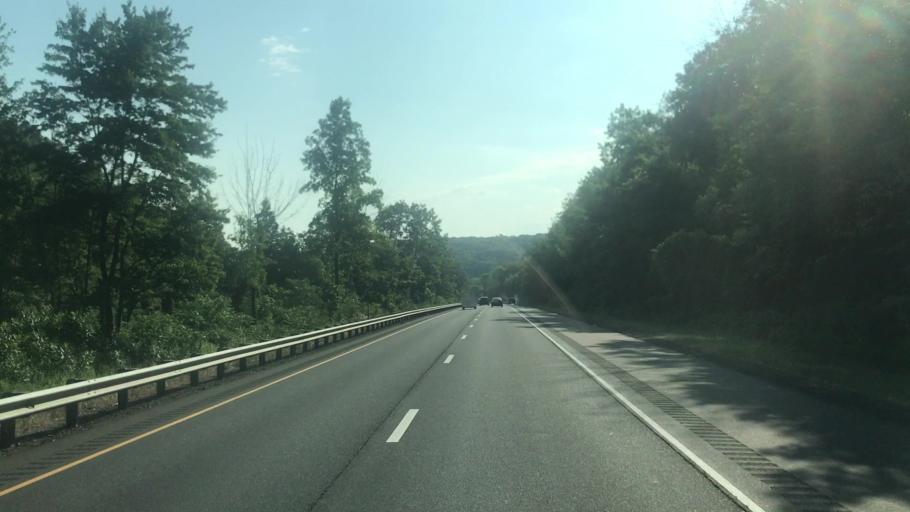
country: US
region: Connecticut
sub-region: New Haven County
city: Southbury
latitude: 41.4918
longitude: -73.1668
